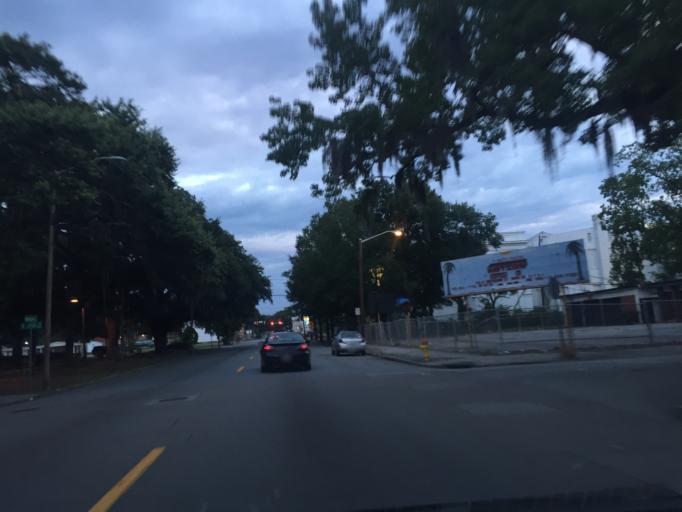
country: US
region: Georgia
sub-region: Chatham County
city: Savannah
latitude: 32.0564
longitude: -81.1051
